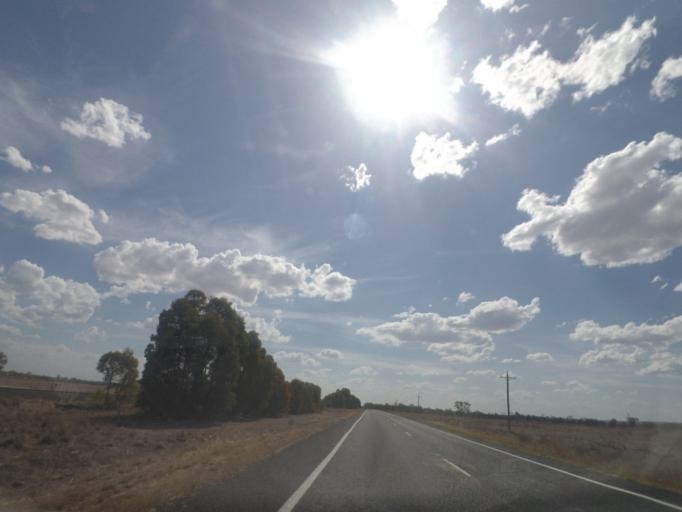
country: AU
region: New South Wales
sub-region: Moree Plains
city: Boggabilla
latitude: -28.4149
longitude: 151.1296
